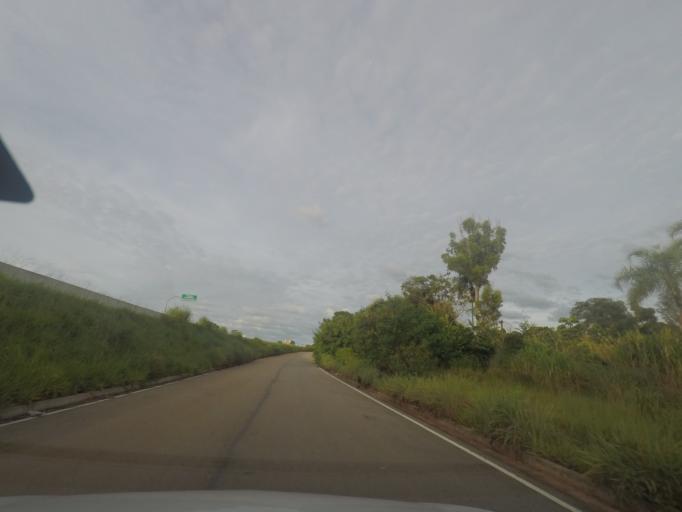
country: BR
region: Goias
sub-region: Trindade
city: Trindade
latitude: -16.7361
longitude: -49.4044
